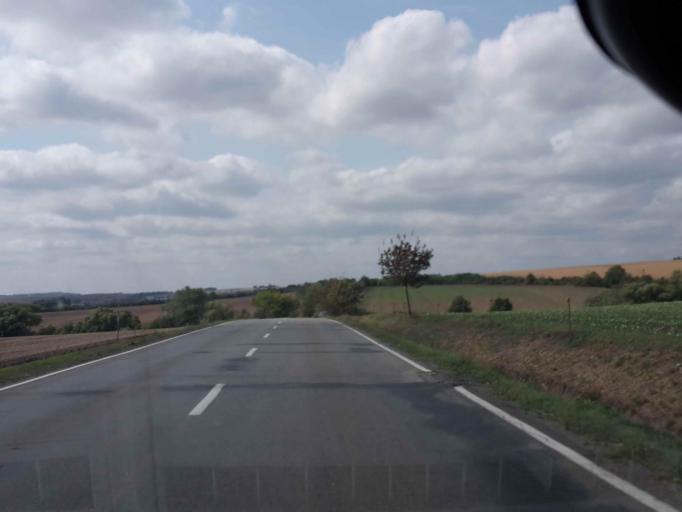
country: CZ
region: South Moravian
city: Rousinov
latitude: 49.1940
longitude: 16.8580
